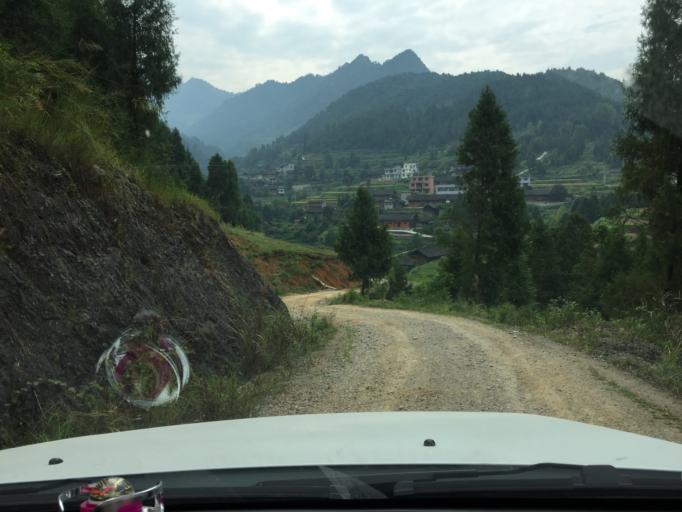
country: CN
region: Guizhou Sheng
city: Dabachang
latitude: 27.7987
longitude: 108.4010
